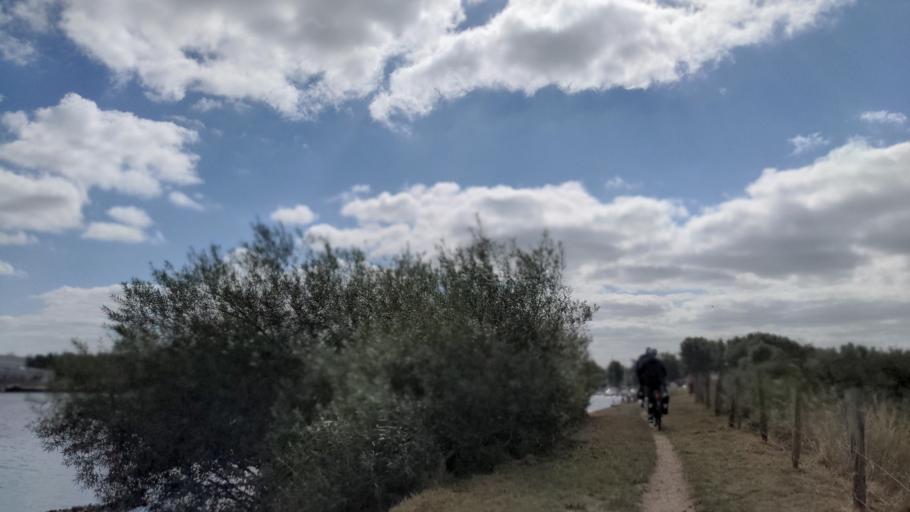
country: DE
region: Schleswig-Holstein
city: Ratekau
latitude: 53.9032
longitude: 10.7633
